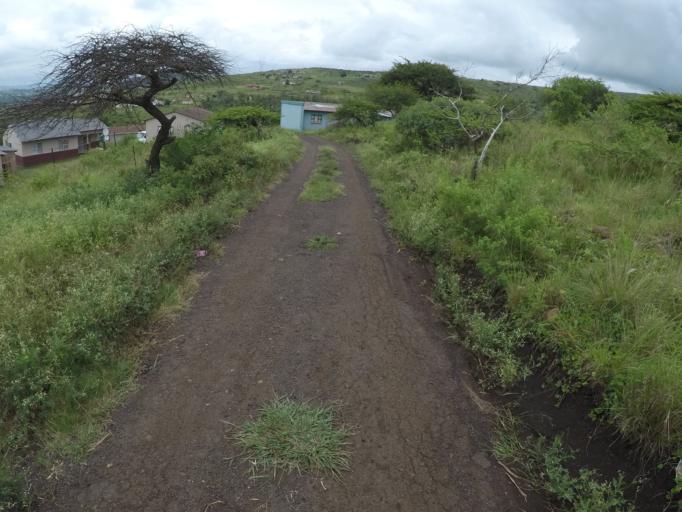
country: ZA
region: KwaZulu-Natal
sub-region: uThungulu District Municipality
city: Empangeni
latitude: -28.7060
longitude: 31.8494
